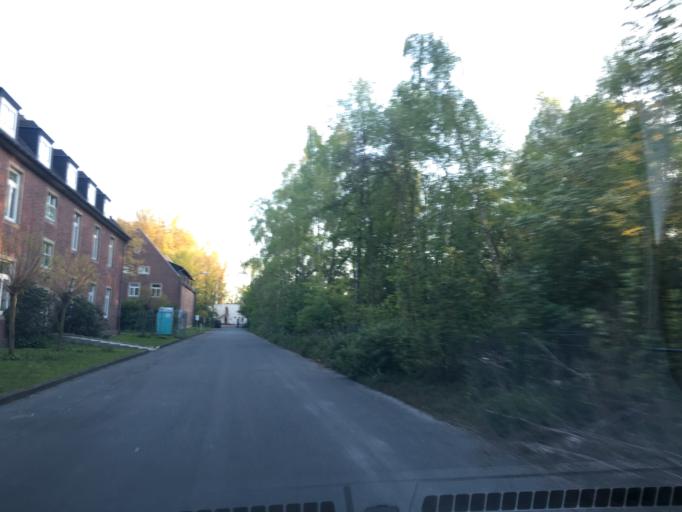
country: DE
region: North Rhine-Westphalia
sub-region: Regierungsbezirk Munster
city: Muenster
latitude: 51.9435
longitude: 7.6434
